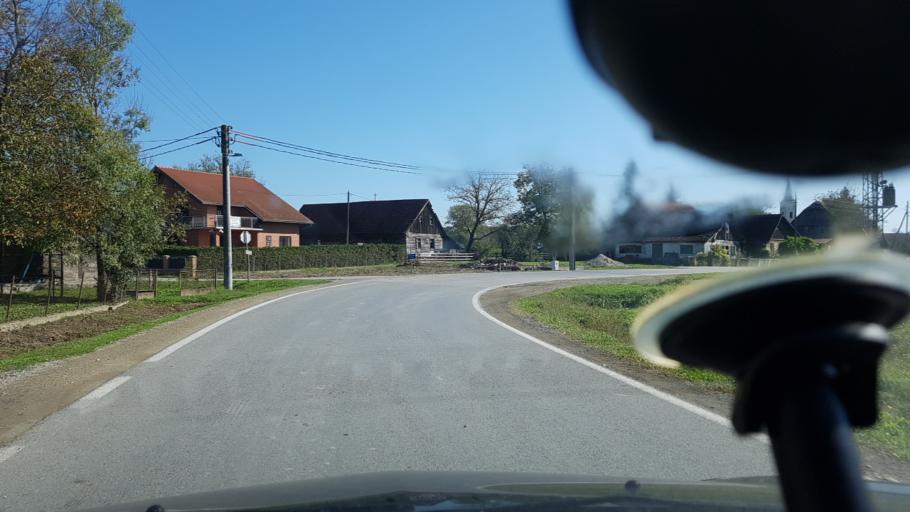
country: HR
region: Zagrebacka
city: Lupoglav
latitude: 45.7167
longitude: 16.3181
